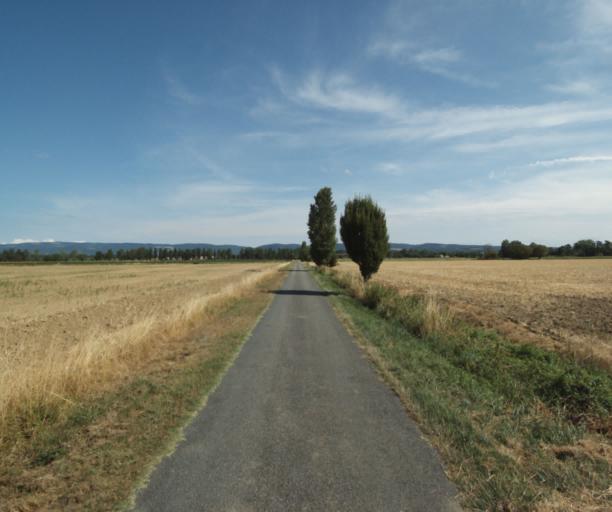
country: FR
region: Midi-Pyrenees
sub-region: Departement de la Haute-Garonne
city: Revel
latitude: 43.4965
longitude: 1.9847
